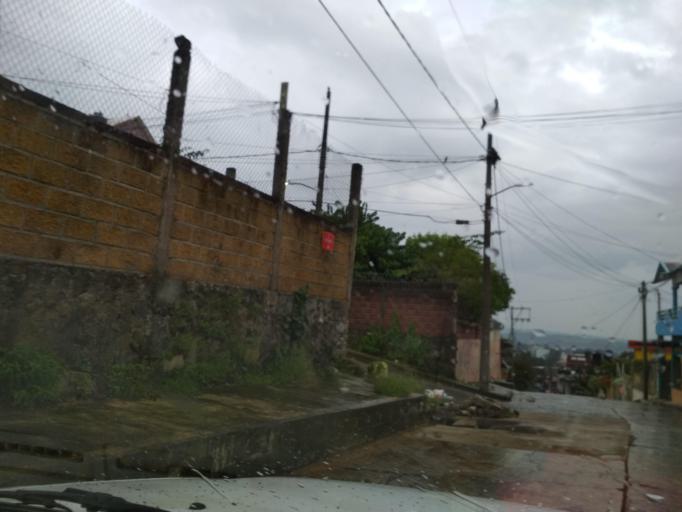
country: MX
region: Veracruz
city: San Andres Tuxtla
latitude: 18.4562
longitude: -95.2155
